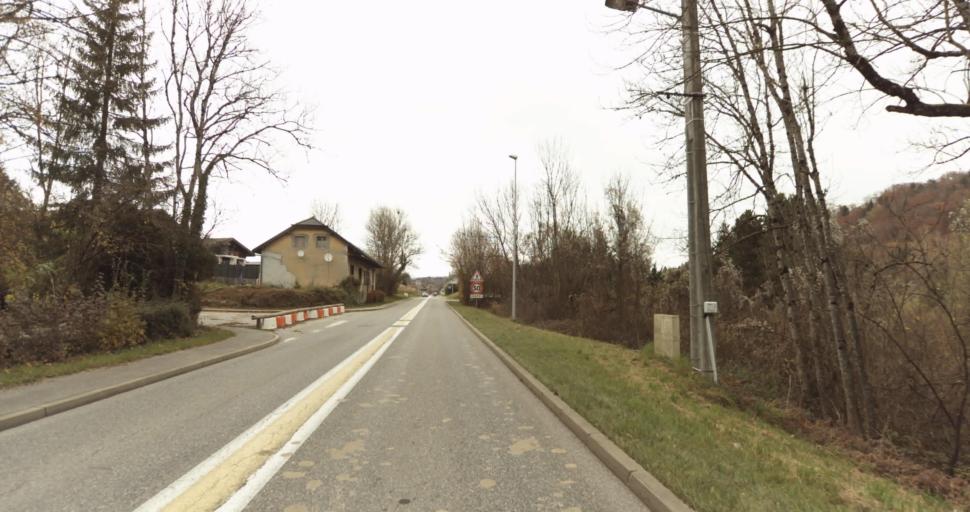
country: FR
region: Rhone-Alpes
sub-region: Departement de la Haute-Savoie
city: Saint-Martin-Bellevue
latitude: 45.9743
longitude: 6.1641
